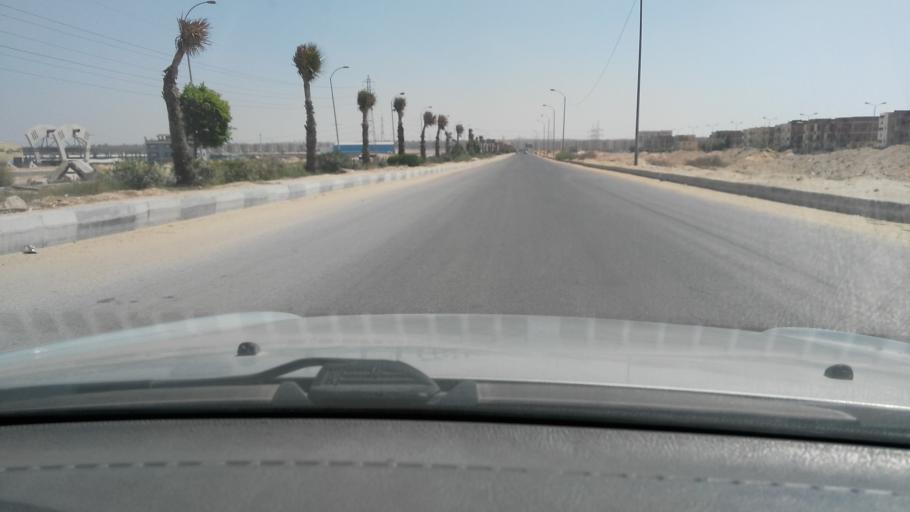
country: EG
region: Al Jizah
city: Madinat Sittah Uktubar
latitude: 29.9069
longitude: 30.9218
